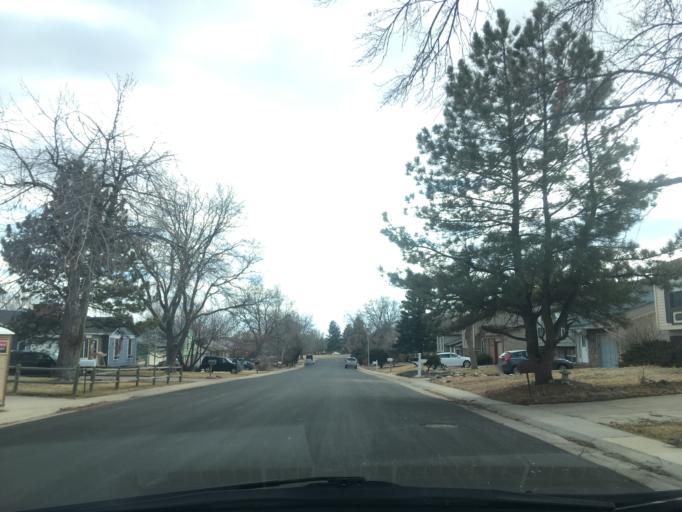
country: US
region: Colorado
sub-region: Broomfield County
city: Broomfield
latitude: 39.9382
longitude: -105.0550
